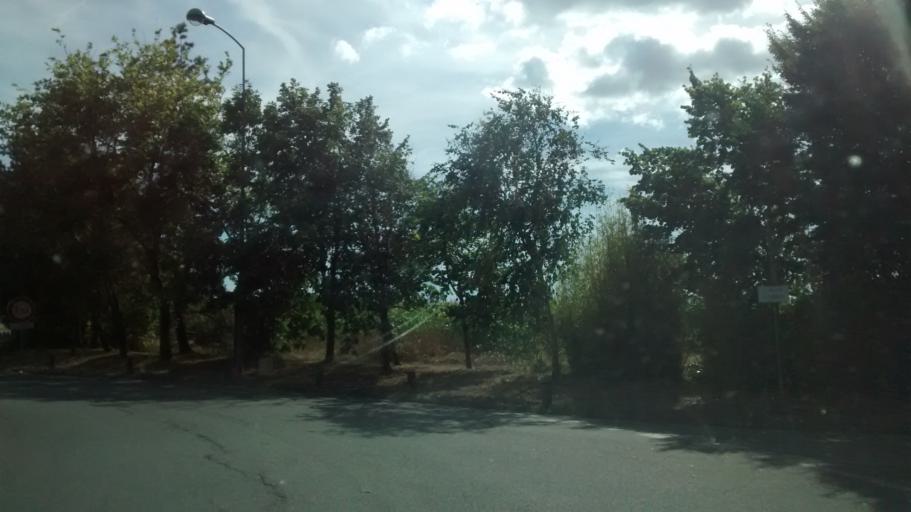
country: FR
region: Pays de la Loire
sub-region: Departement de la Loire-Atlantique
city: Pont-Saint-Martin
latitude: 47.1449
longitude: -1.6043
